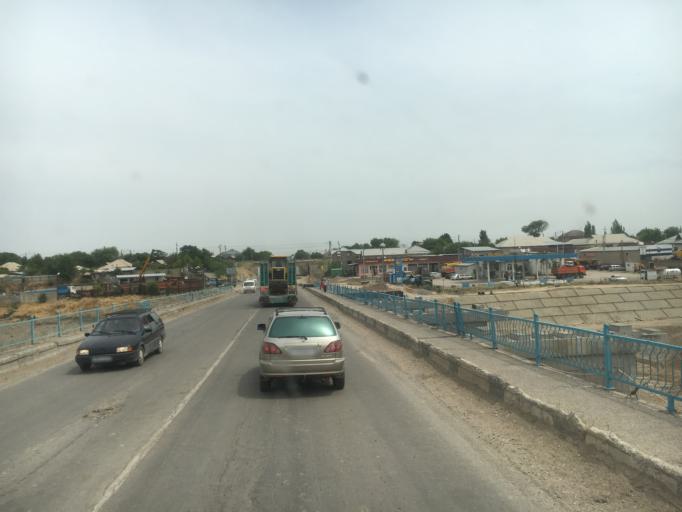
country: KZ
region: Ongtustik Qazaqstan
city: Shymkent
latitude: 42.3323
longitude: 69.5158
